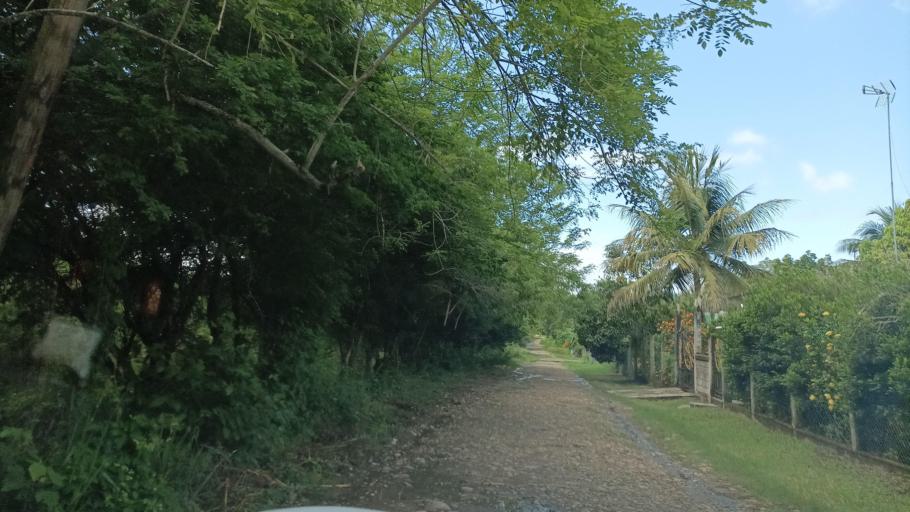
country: MX
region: Veracruz
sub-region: Tantoyuca
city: El Lindero
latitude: 21.1908
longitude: -98.1457
